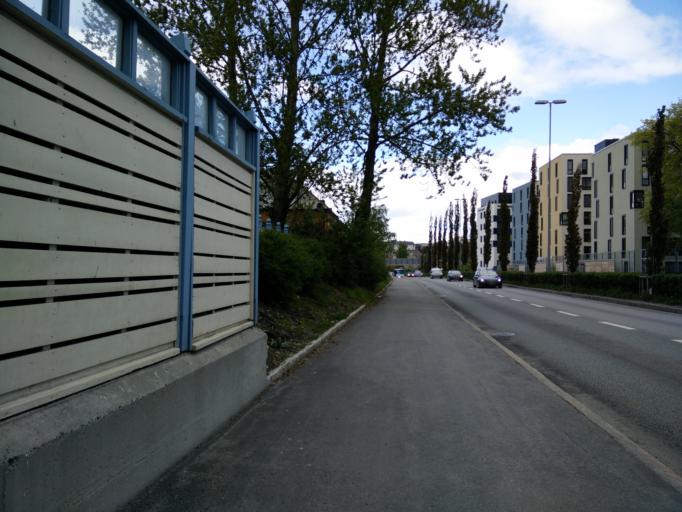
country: NO
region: Sor-Trondelag
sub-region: Trondheim
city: Trondheim
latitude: 63.4107
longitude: 10.3990
